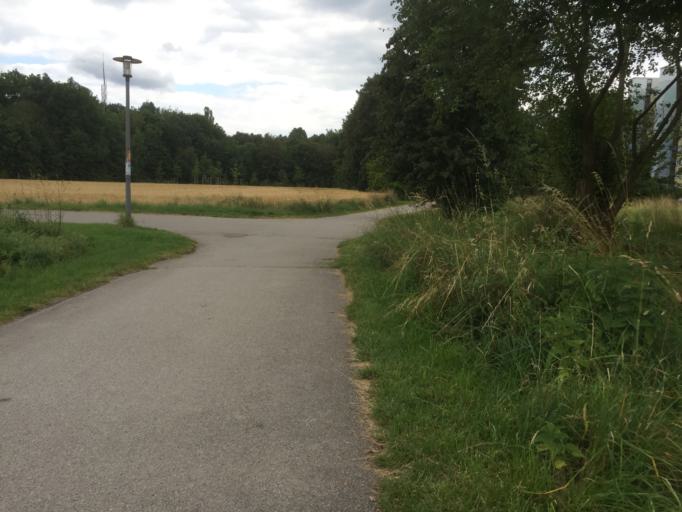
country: DE
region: Bavaria
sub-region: Upper Bavaria
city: Neubiberg
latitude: 48.1083
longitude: 11.6302
